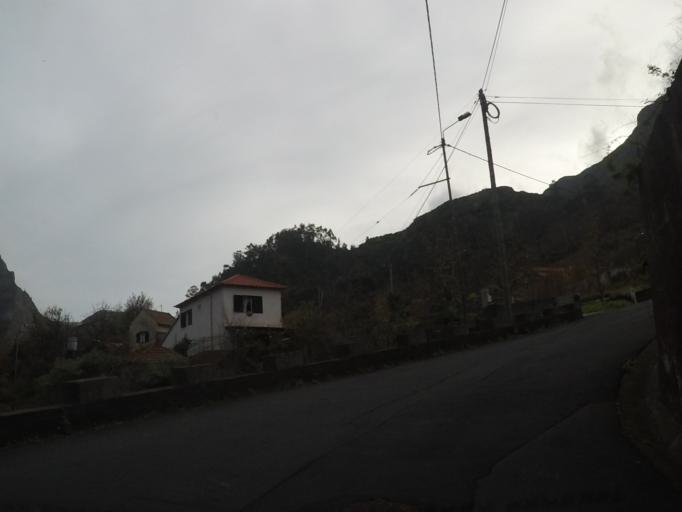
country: PT
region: Madeira
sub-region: Camara de Lobos
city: Curral das Freiras
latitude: 32.7336
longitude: -16.9703
